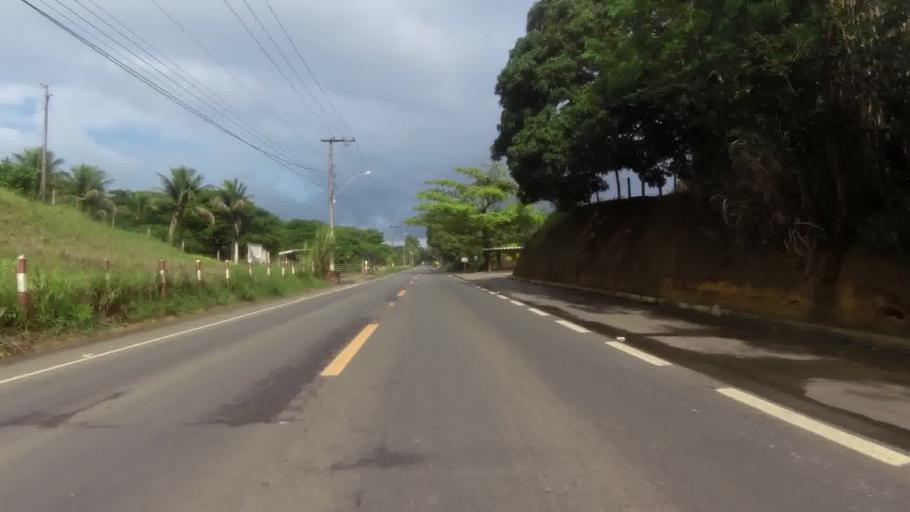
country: BR
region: Espirito Santo
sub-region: Piuma
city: Piuma
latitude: -20.8113
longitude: -40.6831
